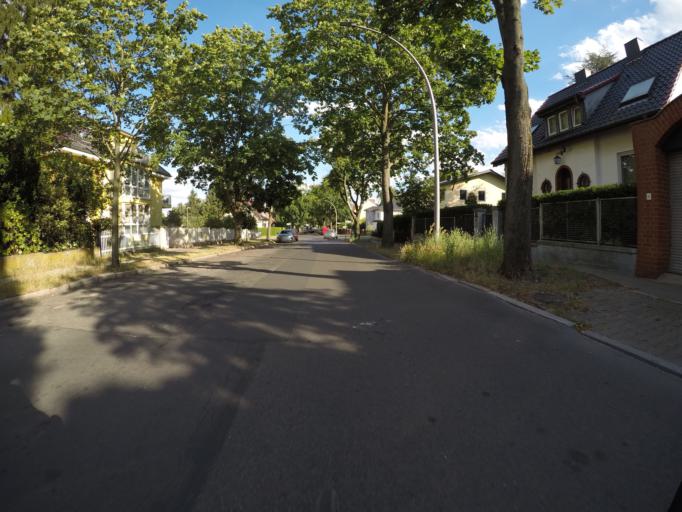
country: DE
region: Berlin
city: Lubars
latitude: 52.6103
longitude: 13.3391
